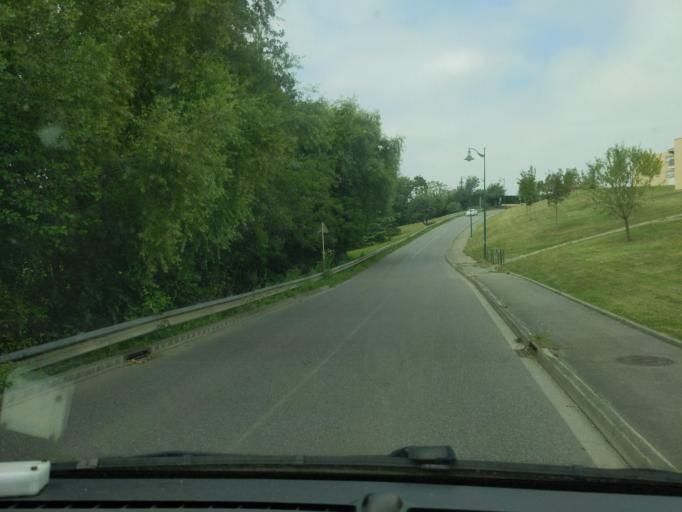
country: FR
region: Midi-Pyrenees
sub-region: Departement de la Haute-Garonne
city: Escalquens
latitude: 43.5207
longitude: 1.5622
